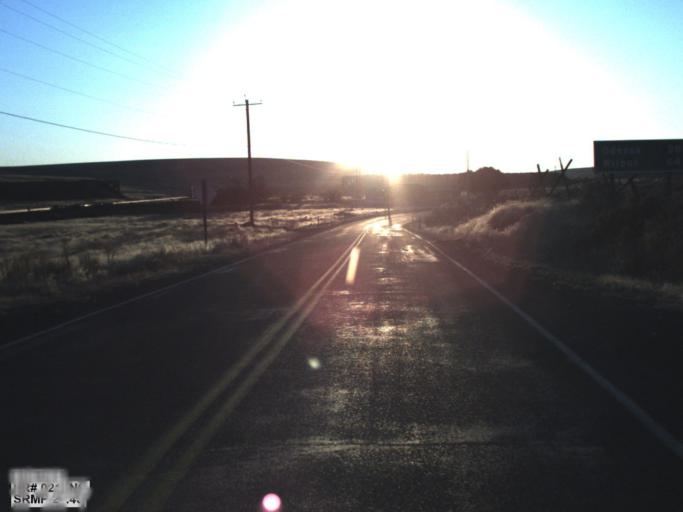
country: US
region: Washington
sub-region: Adams County
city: Ritzville
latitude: 46.9712
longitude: -118.6300
